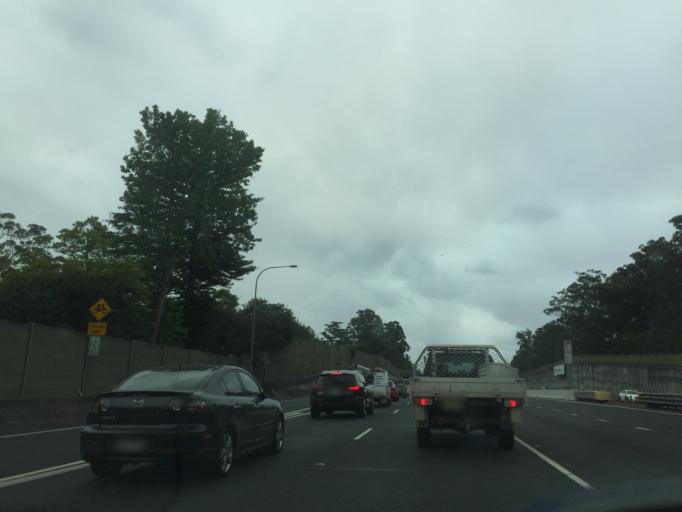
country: AU
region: New South Wales
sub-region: Hornsby Shire
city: Beecroft
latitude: -33.7579
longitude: 151.0546
